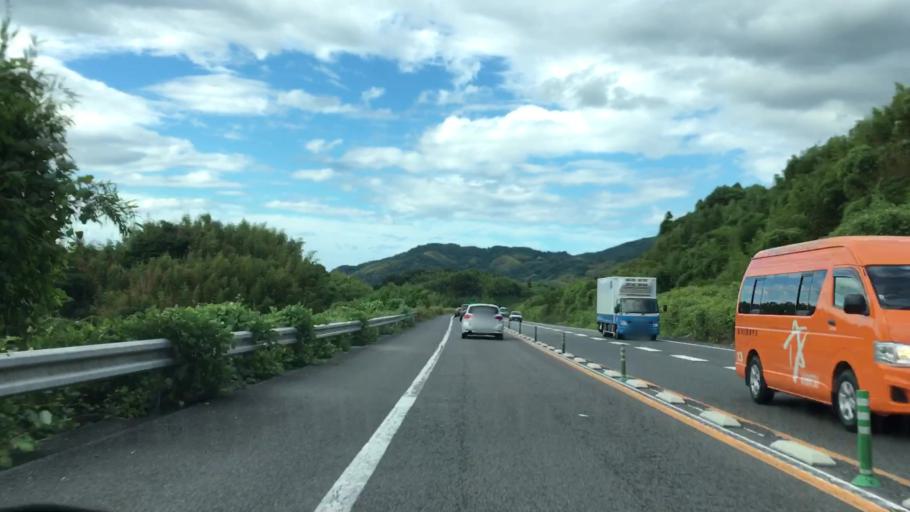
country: JP
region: Saga Prefecture
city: Karatsu
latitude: 33.4340
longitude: 130.0483
